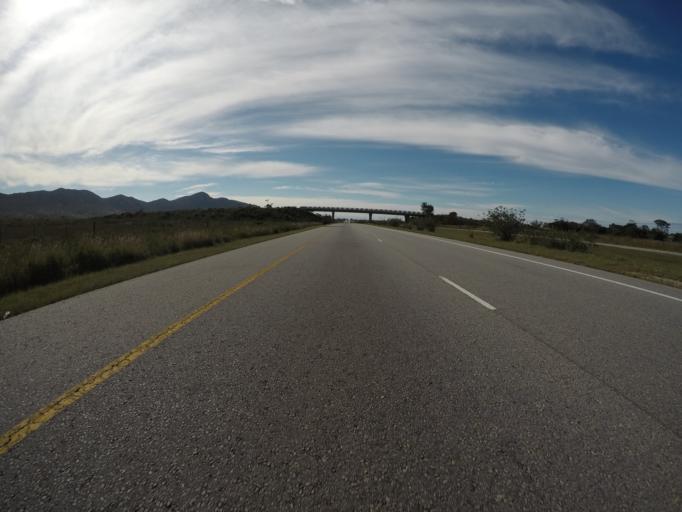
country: ZA
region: Eastern Cape
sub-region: Nelson Mandela Bay Metropolitan Municipality
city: Uitenhage
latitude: -33.9099
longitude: 25.2175
